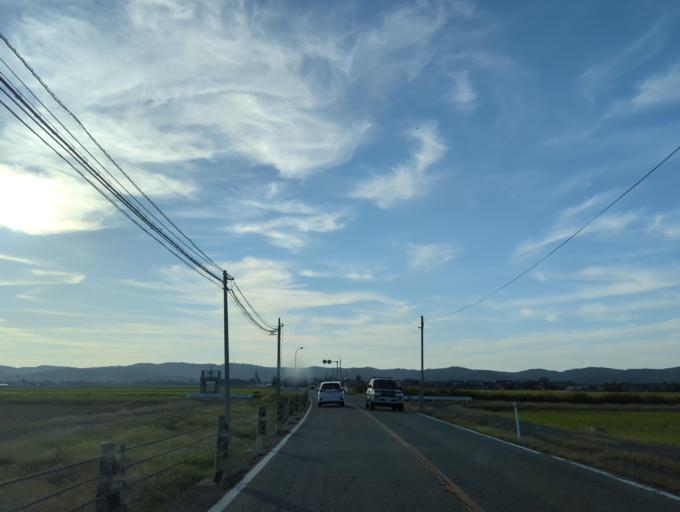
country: JP
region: Niigata
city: Mitsuke
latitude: 37.5554
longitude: 138.8441
